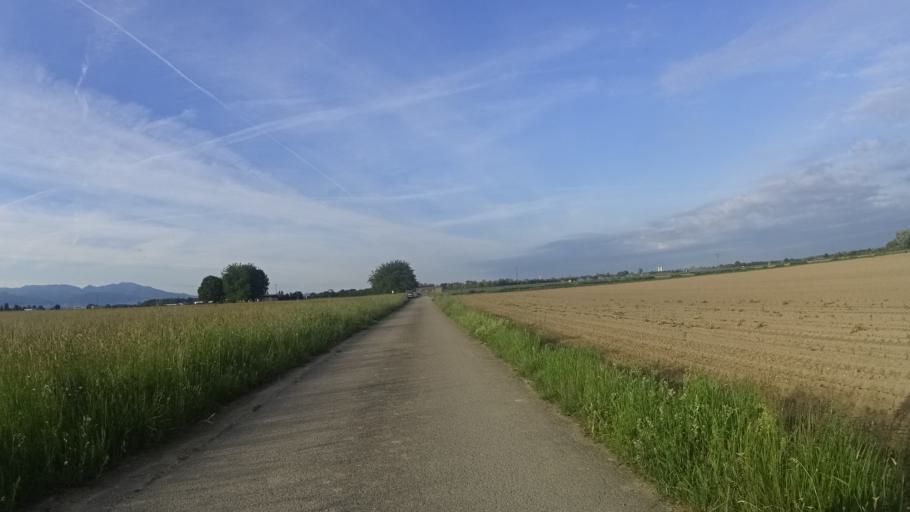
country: DE
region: Baden-Wuerttemberg
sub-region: Freiburg Region
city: Hartheim
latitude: 47.9542
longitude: 7.6495
